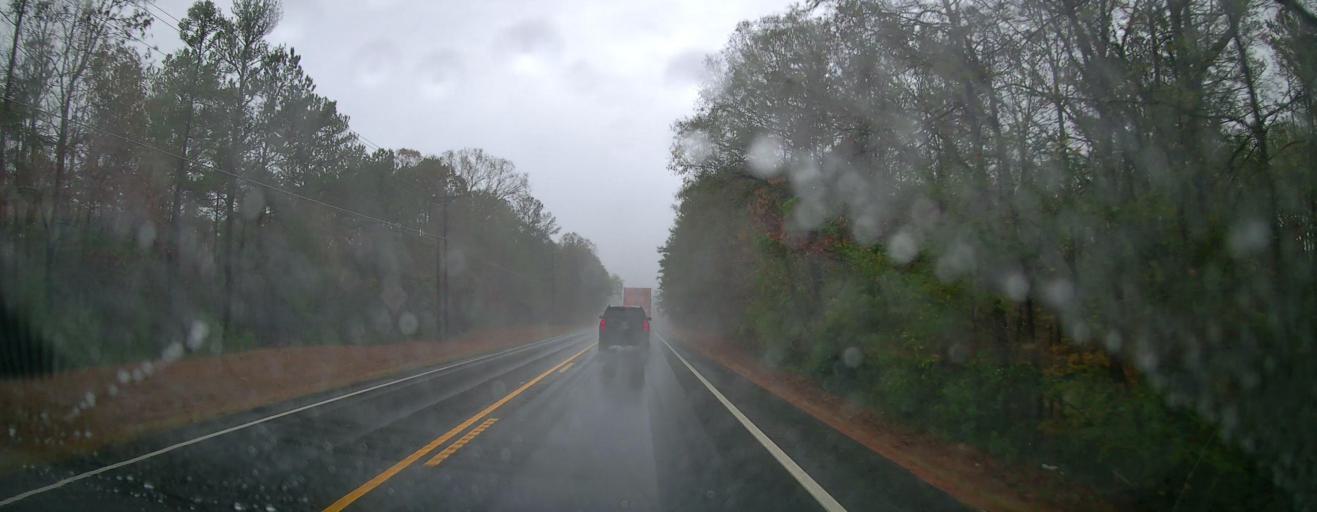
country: US
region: Georgia
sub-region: Putnam County
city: Eatonton
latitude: 33.2123
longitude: -83.4336
